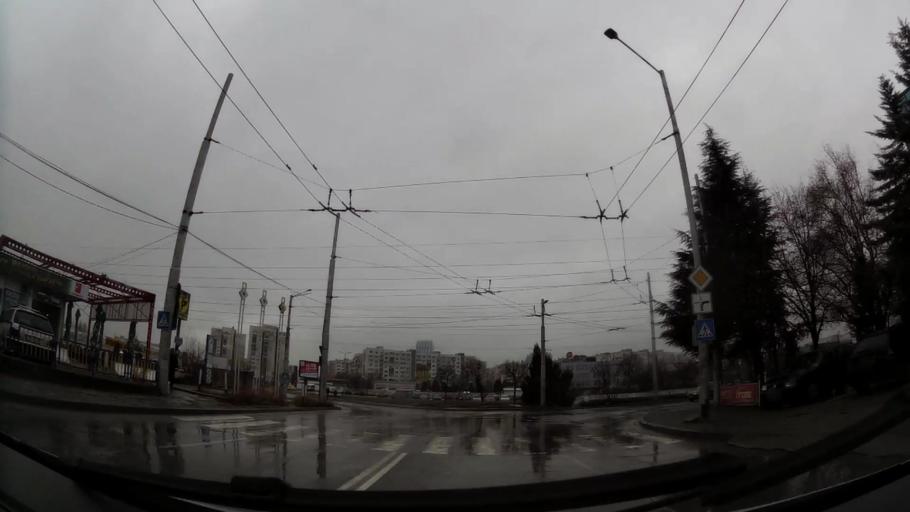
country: BG
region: Sofia-Capital
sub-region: Stolichna Obshtina
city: Sofia
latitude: 42.6568
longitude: 23.4012
